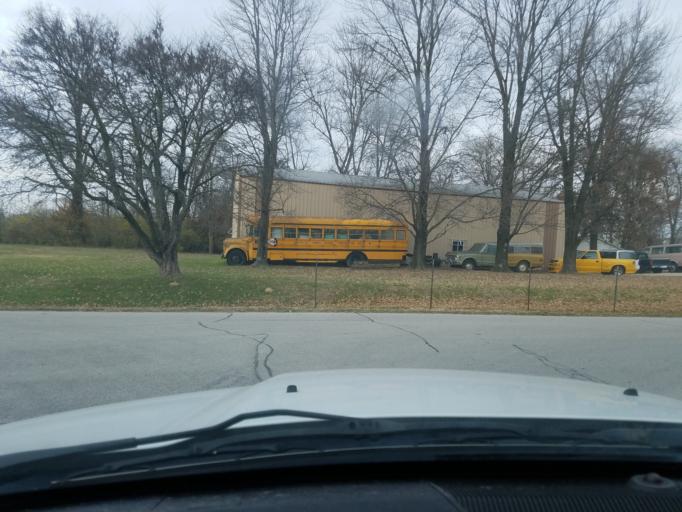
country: US
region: Indiana
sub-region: Dubois County
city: Ferdinand
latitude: 38.2195
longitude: -86.8665
